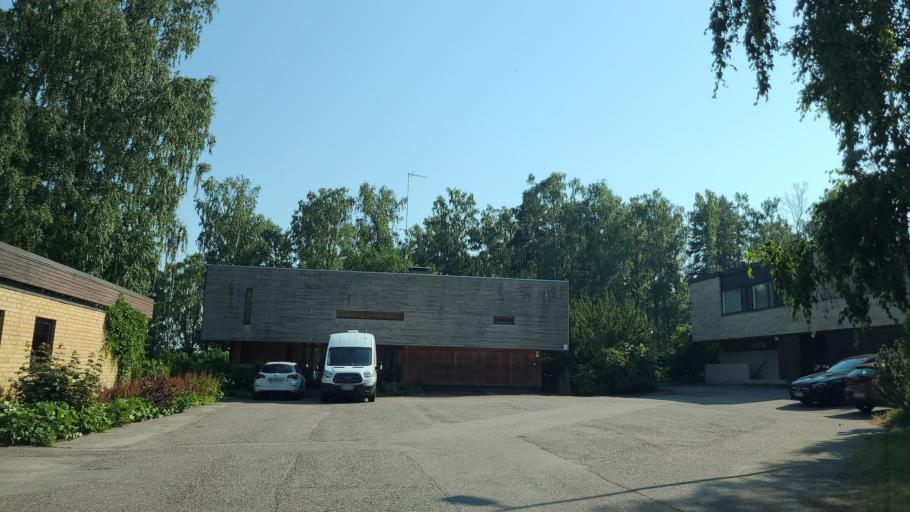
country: FI
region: Uusimaa
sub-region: Helsinki
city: Teekkarikylae
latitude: 60.1786
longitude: 24.8564
